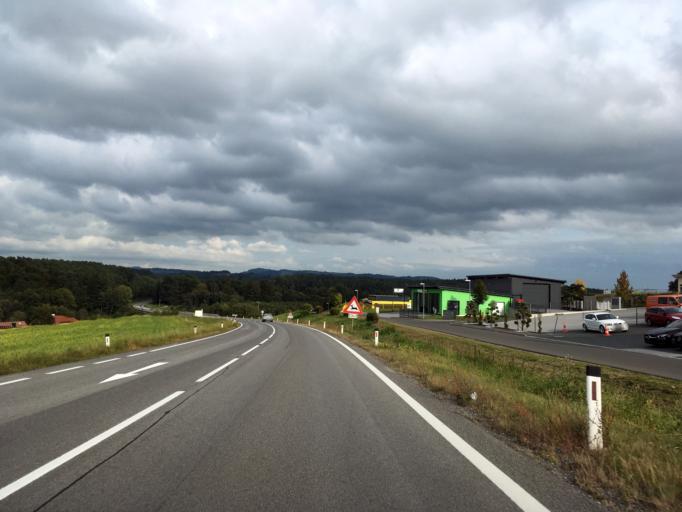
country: AT
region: Styria
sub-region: Politischer Bezirk Hartberg-Fuerstenfeld
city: Dechantskirchen
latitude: 47.4146
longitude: 16.0223
